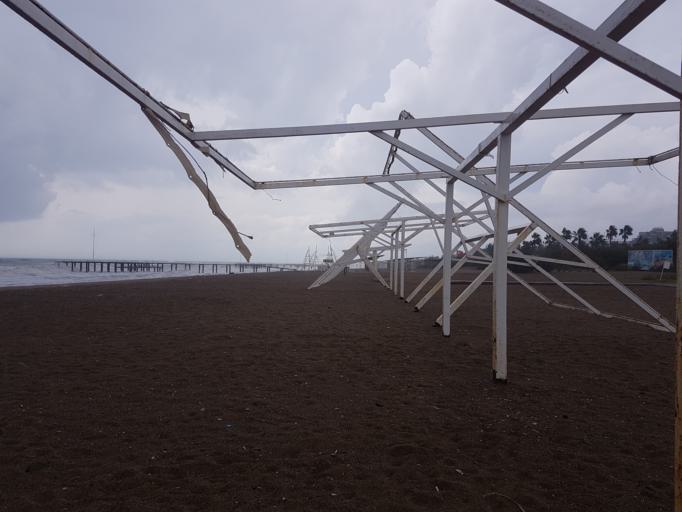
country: TR
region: Antalya
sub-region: Serik
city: Kumkoey
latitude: 36.8534
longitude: 30.8875
